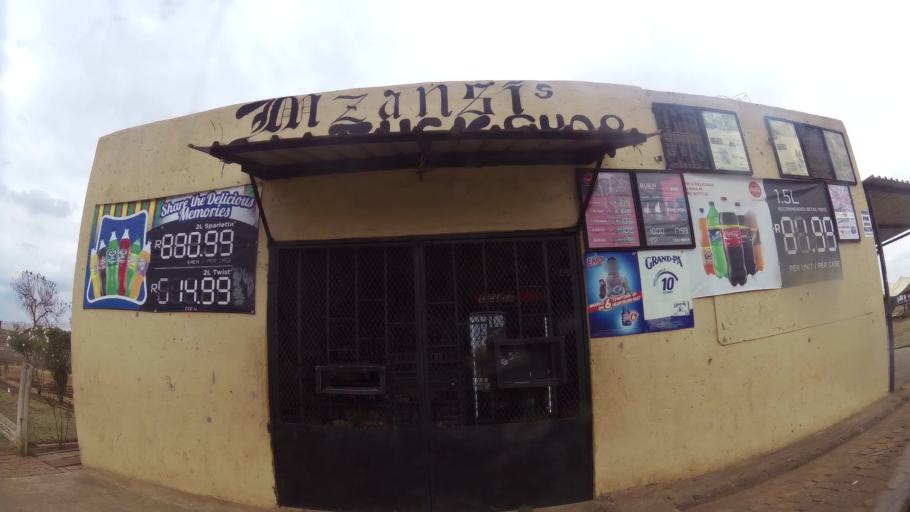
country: ZA
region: Gauteng
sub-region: Ekurhuleni Metropolitan Municipality
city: Germiston
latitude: -26.3885
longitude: 28.1177
